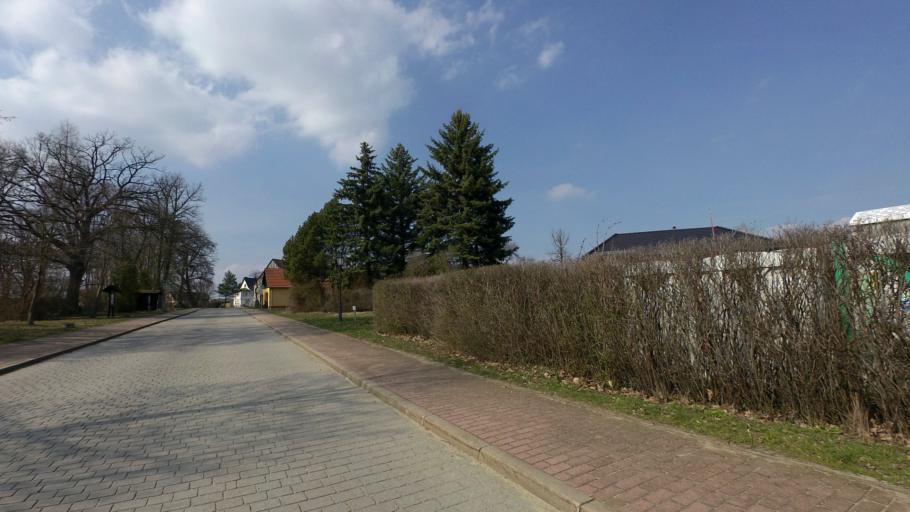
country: DE
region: Brandenburg
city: Dahme
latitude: 51.9412
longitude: 13.4441
